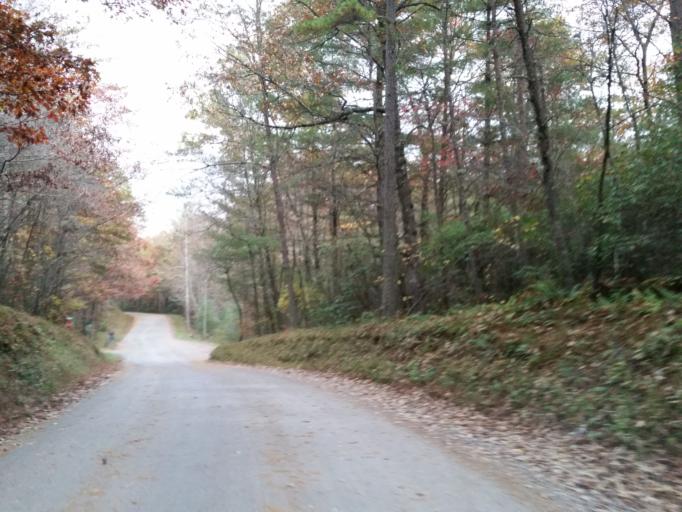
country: US
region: Georgia
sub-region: Fannin County
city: Blue Ridge
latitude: 34.7273
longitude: -84.2062
